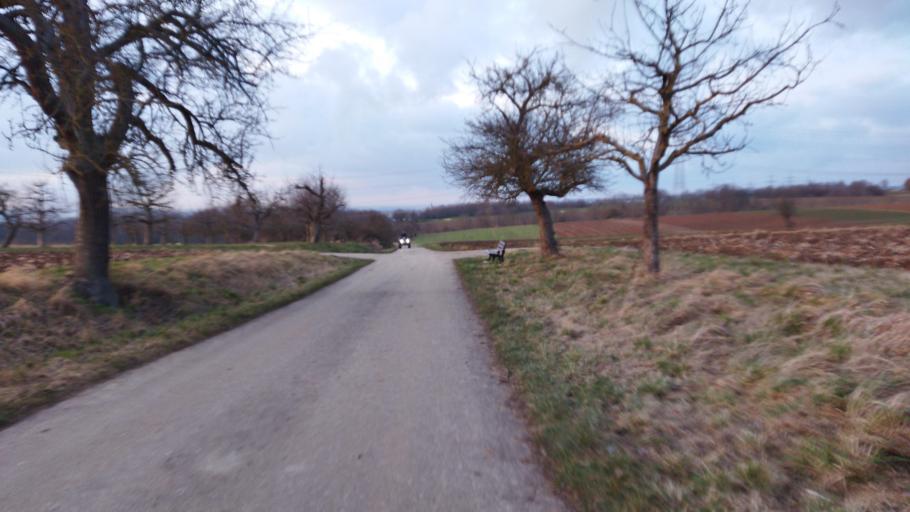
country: DE
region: Baden-Wuerttemberg
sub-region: Regierungsbezirk Stuttgart
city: Neckarwestheim
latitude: 49.0257
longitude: 9.1962
